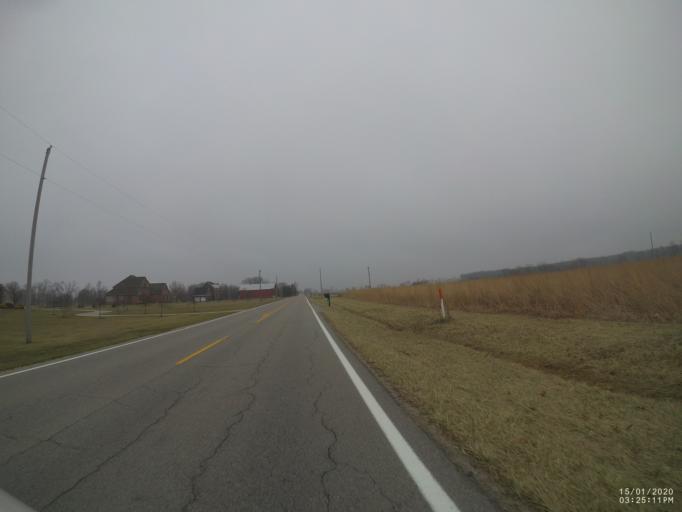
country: US
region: Ohio
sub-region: Sandusky County
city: Woodville
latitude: 41.4302
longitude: -83.4044
